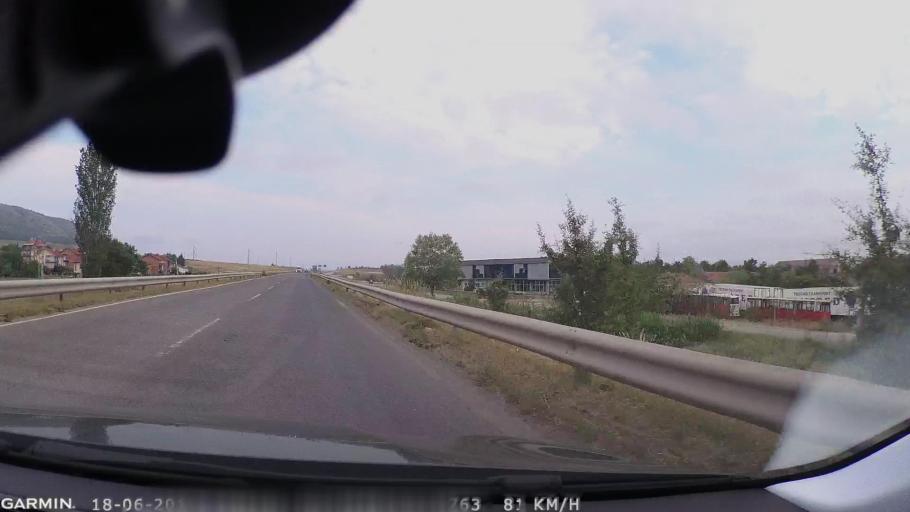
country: MK
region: Stip
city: Shtip
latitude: 41.7752
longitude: 22.1367
